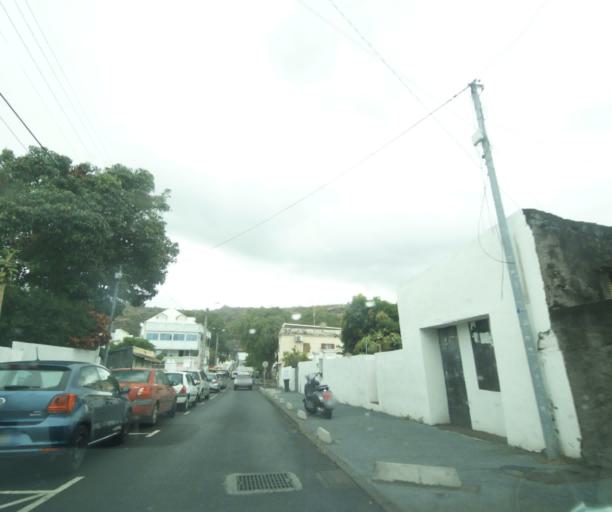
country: RE
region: Reunion
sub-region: Reunion
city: Saint-Paul
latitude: -21.0109
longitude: 55.2698
